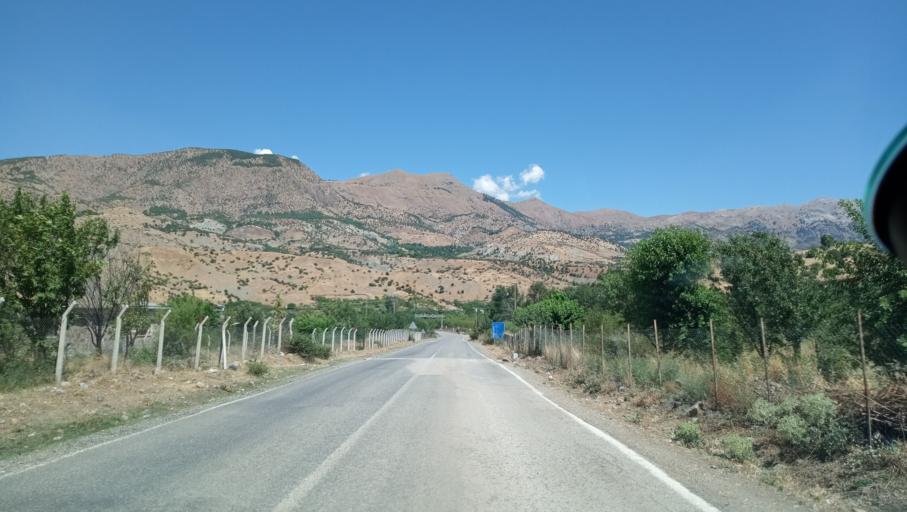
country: TR
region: Diyarbakir
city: Kulp
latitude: 38.4990
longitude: 41.0461
